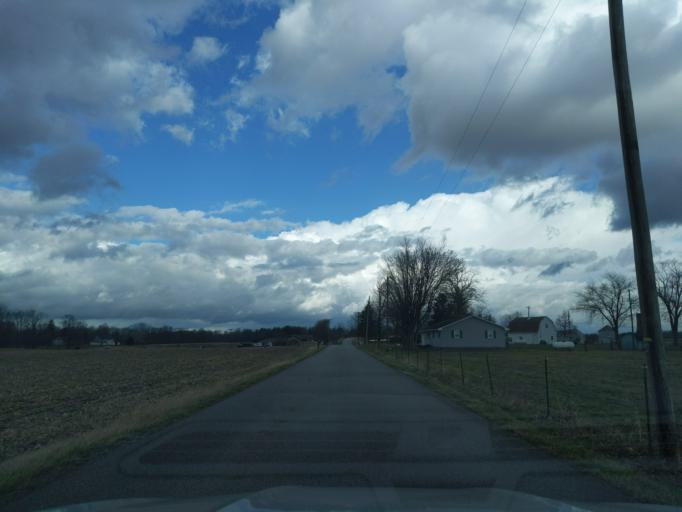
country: US
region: Indiana
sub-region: Decatur County
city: Saint Paul
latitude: 39.3998
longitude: -85.5598
